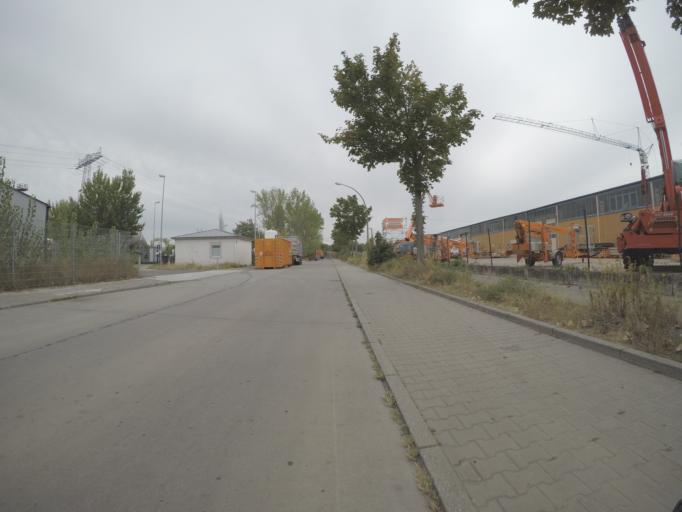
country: DE
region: Berlin
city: Alt-Hohenschoenhausen
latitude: 52.5431
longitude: 13.5266
